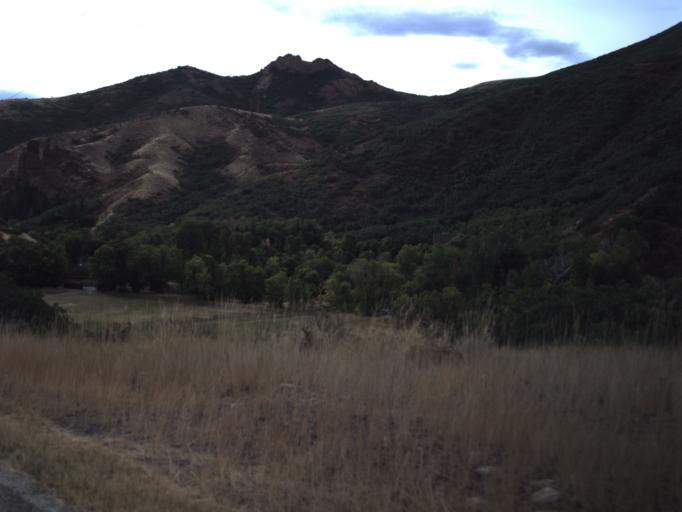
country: US
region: Utah
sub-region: Morgan County
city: Morgan
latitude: 40.9267
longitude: -111.6137
